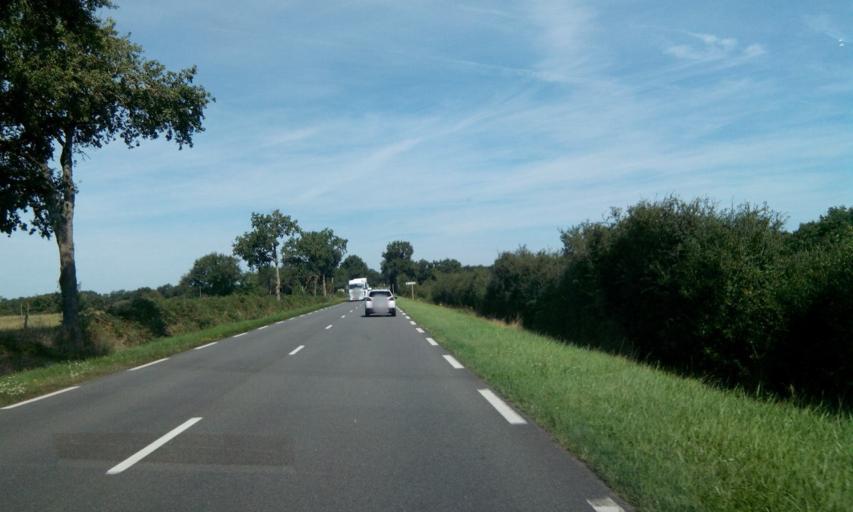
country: FR
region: Poitou-Charentes
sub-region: Departement de la Vienne
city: Availles-Limouzine
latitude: 46.0670
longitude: 0.5982
